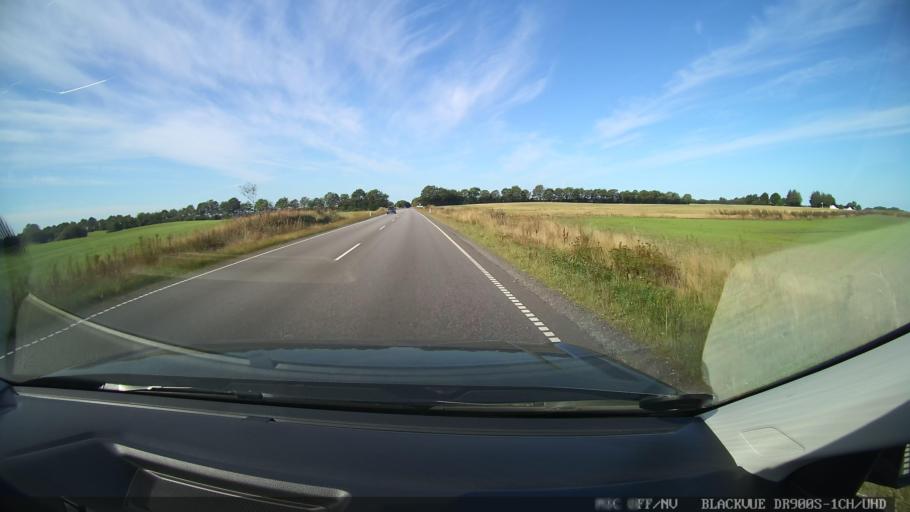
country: DK
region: North Denmark
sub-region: Mariagerfjord Kommune
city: Hobro
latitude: 56.6670
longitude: 9.7602
